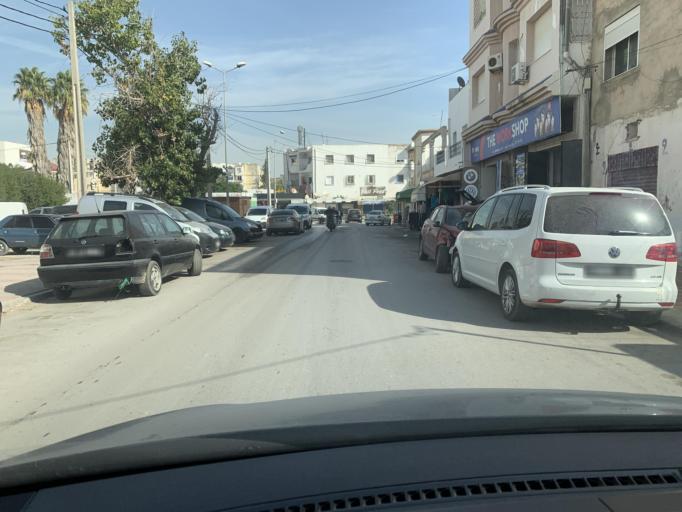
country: TN
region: Manouba
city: Manouba
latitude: 36.8219
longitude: 10.1179
